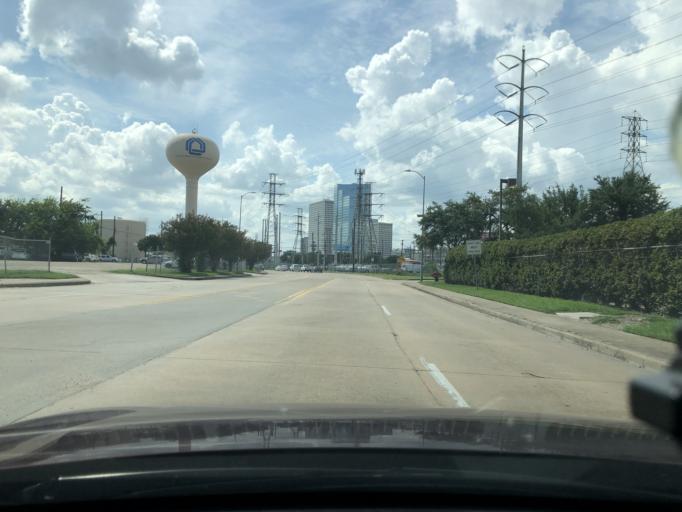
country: US
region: Texas
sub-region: Harris County
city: West University Place
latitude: 29.7289
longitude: -95.4204
